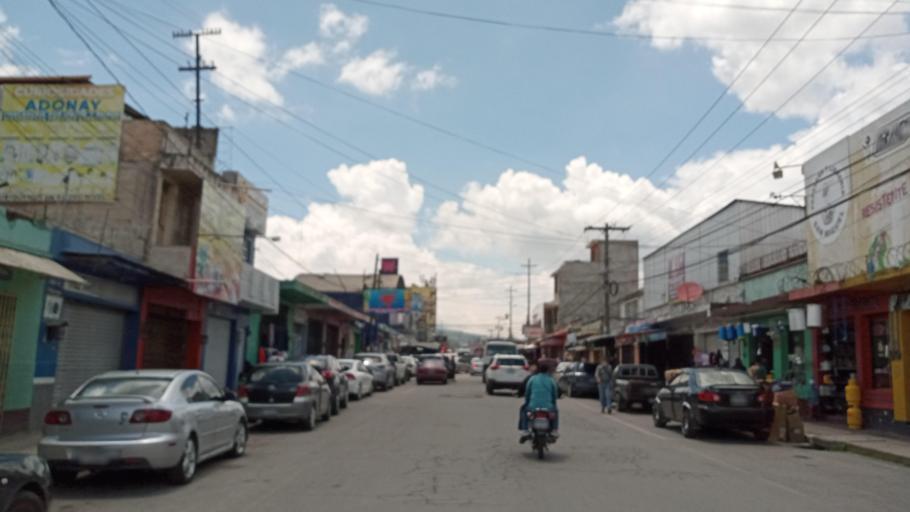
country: GT
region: Quetzaltenango
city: Quetzaltenango
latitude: 14.8413
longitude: -91.5187
